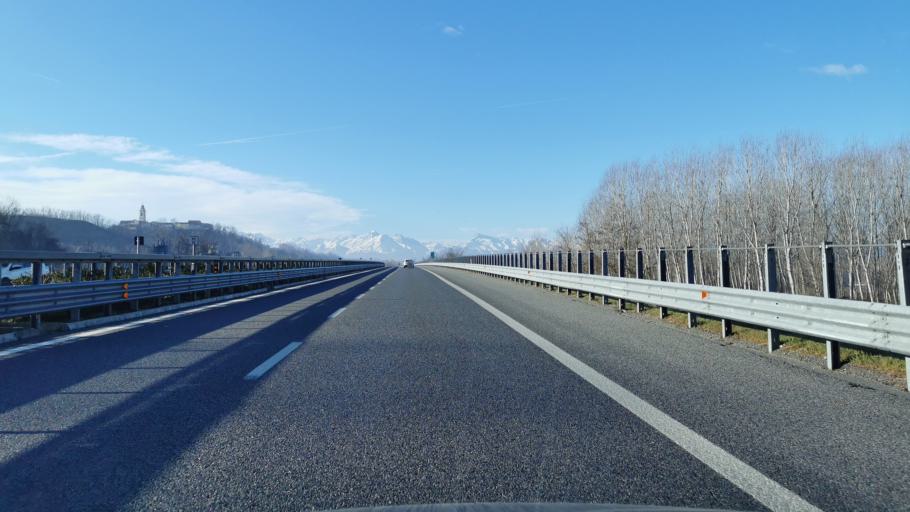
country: IT
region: Piedmont
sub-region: Provincia di Cuneo
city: Montanera
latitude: 44.4699
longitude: 7.6700
